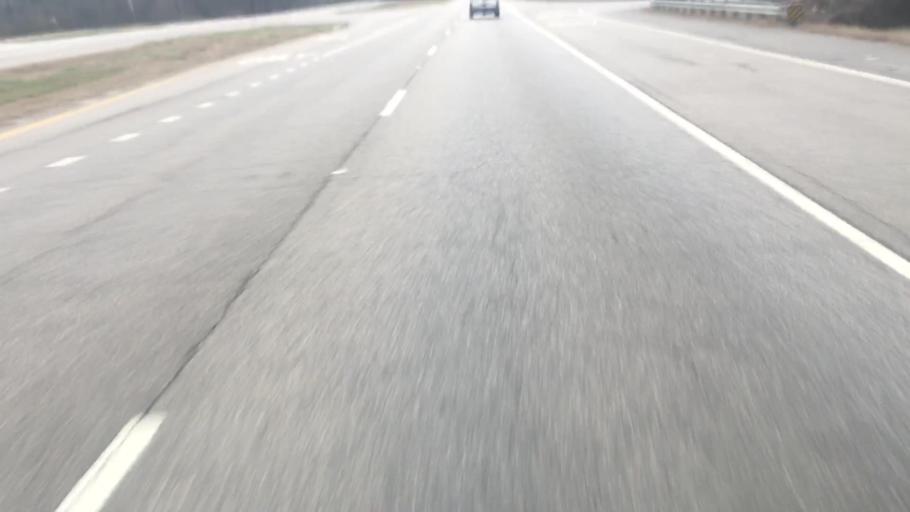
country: US
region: Alabama
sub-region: Walker County
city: Sumiton
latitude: 33.7143
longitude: -86.9960
